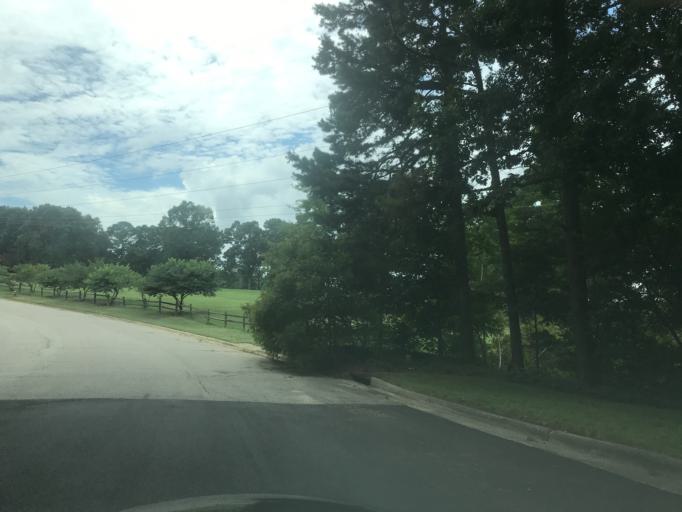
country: US
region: North Carolina
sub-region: Wake County
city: West Raleigh
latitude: 35.8889
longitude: -78.6075
